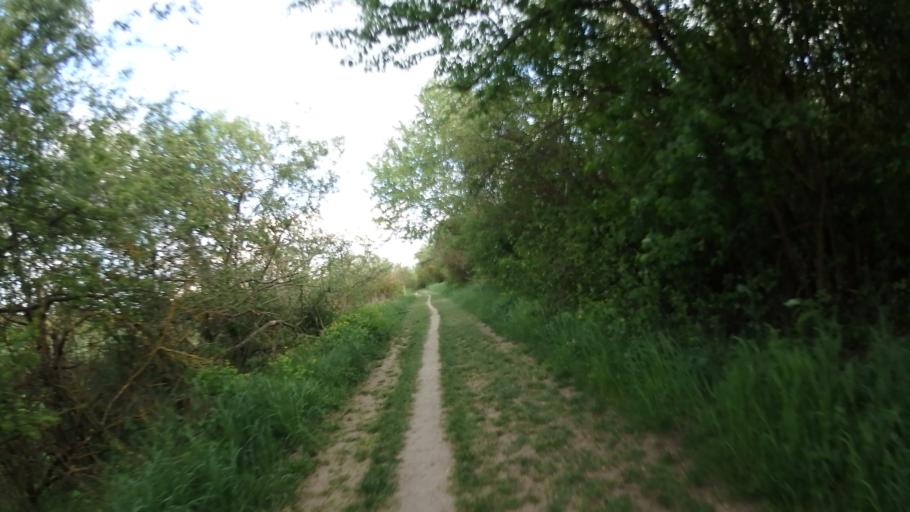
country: CZ
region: South Moravian
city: Moravany
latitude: 49.1584
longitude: 16.5752
